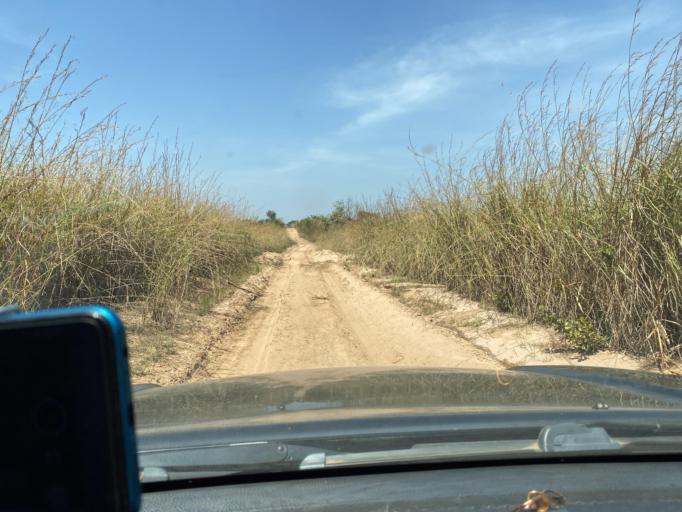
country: CD
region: Kasai-Oriental
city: Kabinda
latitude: -5.8772
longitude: 24.8636
